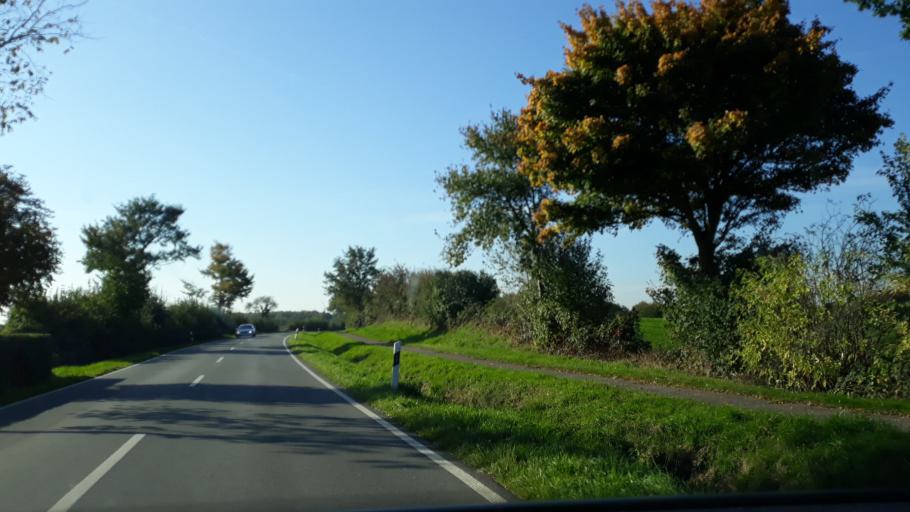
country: DE
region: Schleswig-Holstein
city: Ulsby
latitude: 54.6169
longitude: 9.5915
